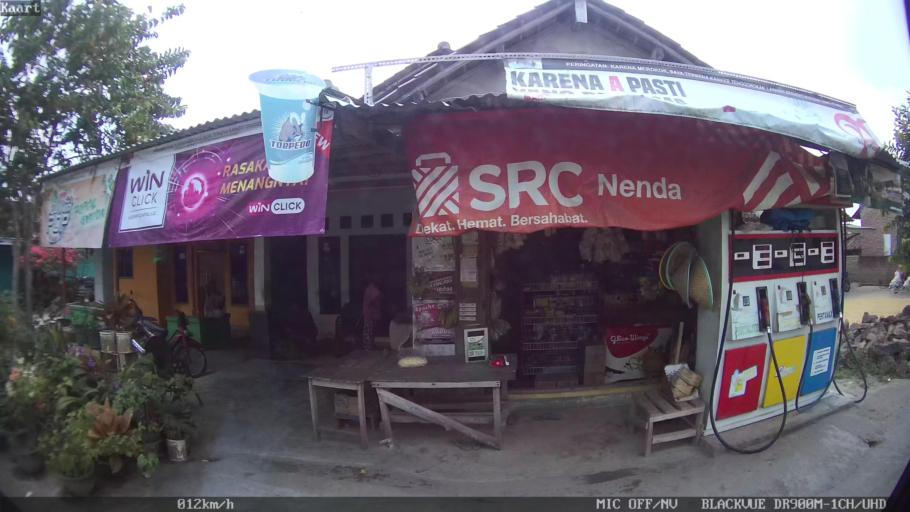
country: ID
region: Lampung
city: Pringsewu
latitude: -5.3482
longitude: 104.9902
